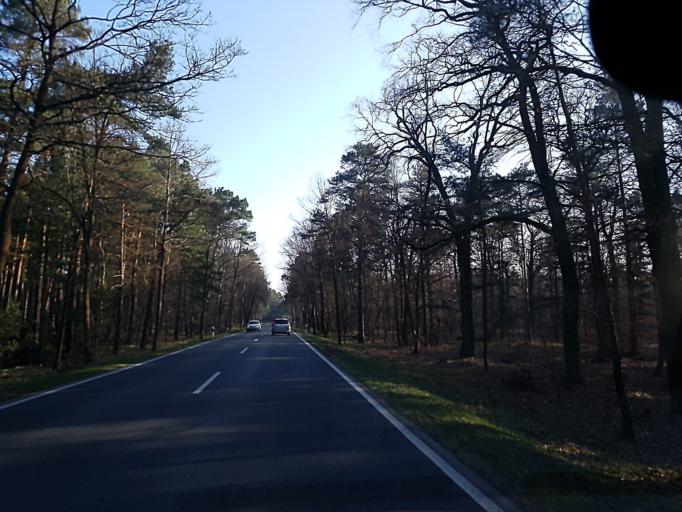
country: DE
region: Brandenburg
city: Calau
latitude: 51.7171
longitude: 13.9233
